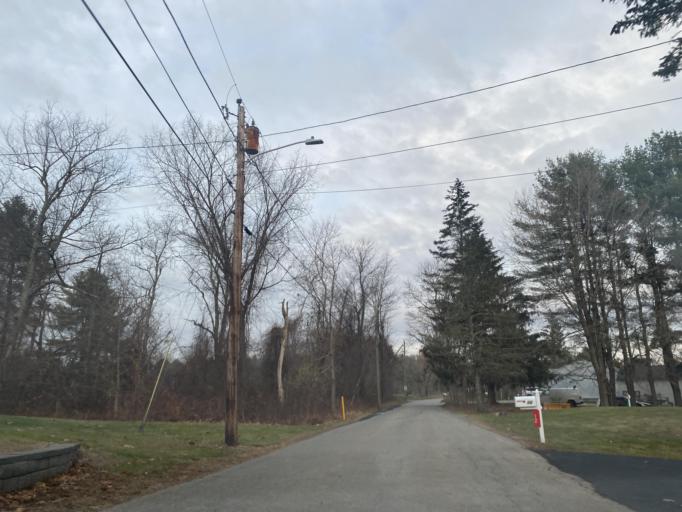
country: US
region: Massachusetts
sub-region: Worcester County
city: Spencer
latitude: 42.2580
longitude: -71.9589
